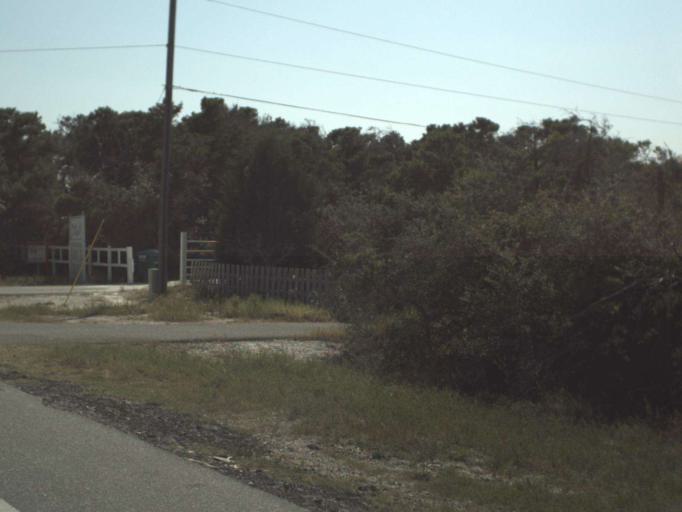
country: US
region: Florida
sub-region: Gulf County
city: Port Saint Joe
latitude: 29.7027
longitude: -85.3777
